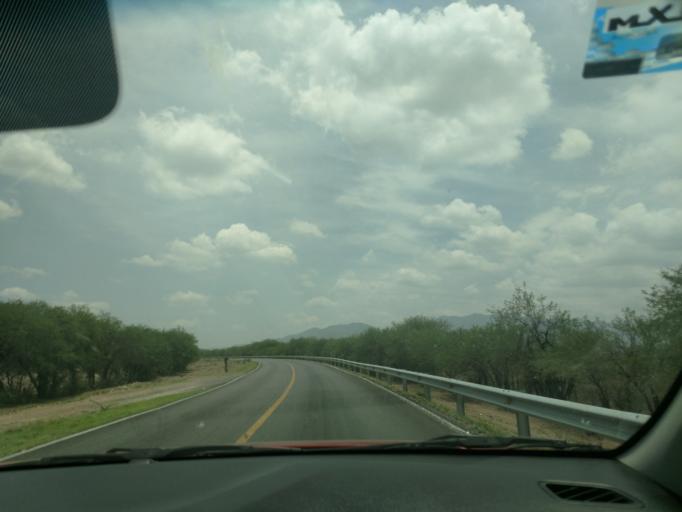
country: MX
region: San Luis Potosi
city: Zaragoza
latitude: 22.0196
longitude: -100.4004
